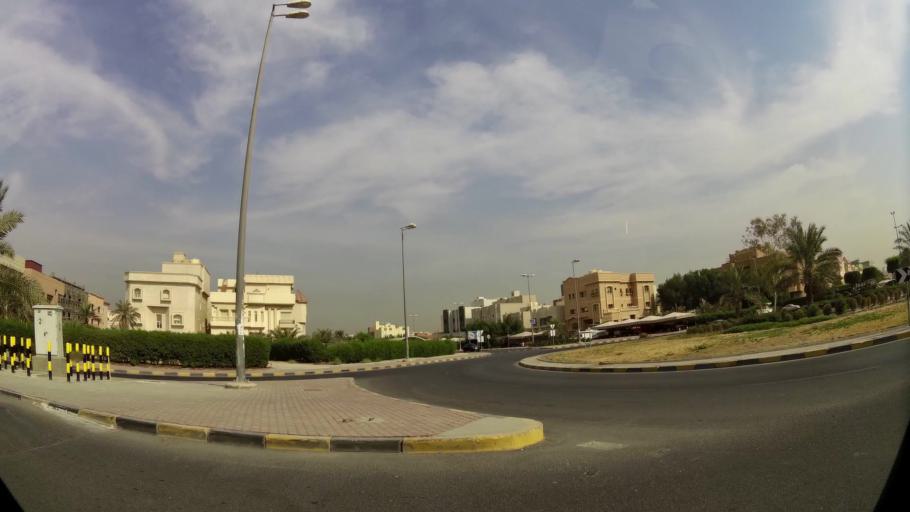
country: KW
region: Al Farwaniyah
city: Janub as Surrah
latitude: 29.2718
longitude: 48.0014
